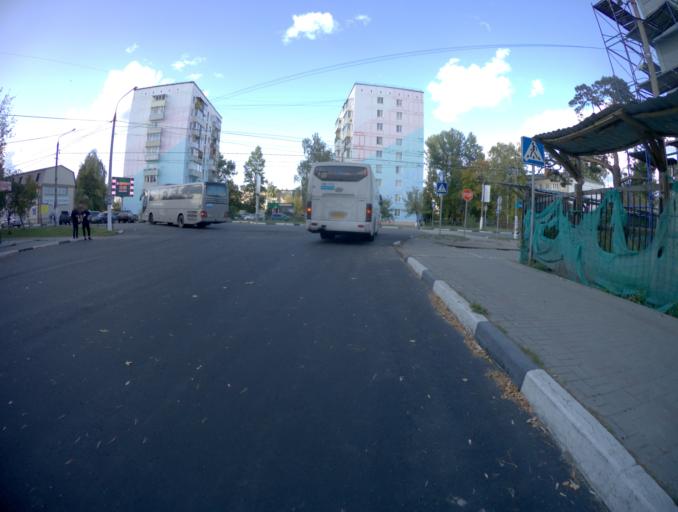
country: RU
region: Moskovskaya
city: Shatura
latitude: 55.5752
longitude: 39.5264
